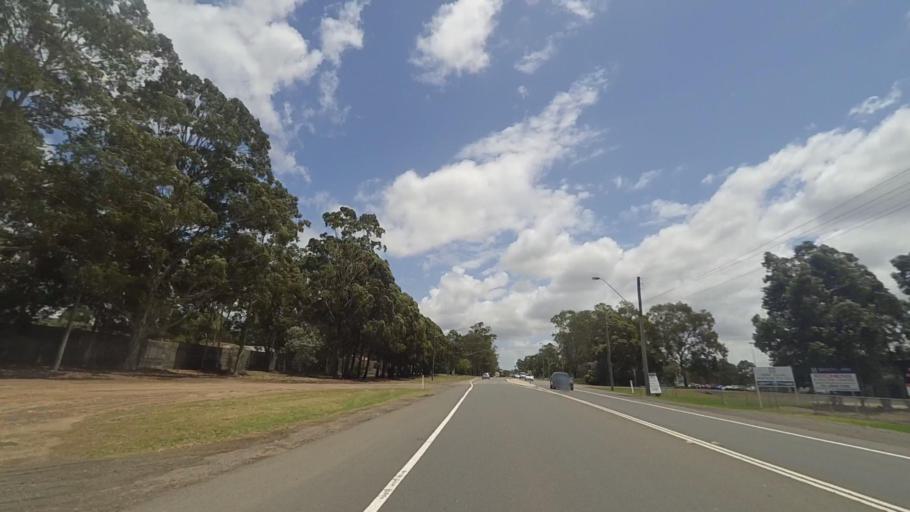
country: AU
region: New South Wales
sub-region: Liverpool
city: Holsworthy
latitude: -33.9570
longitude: 150.9569
